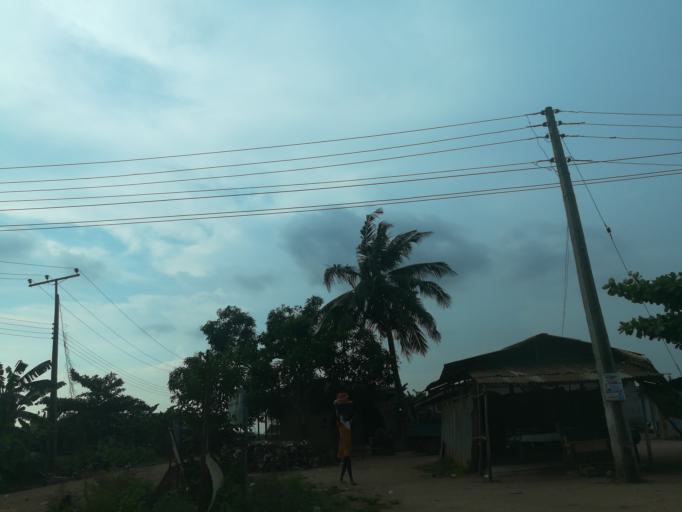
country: NG
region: Lagos
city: Ikorodu
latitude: 6.6117
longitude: 3.5970
